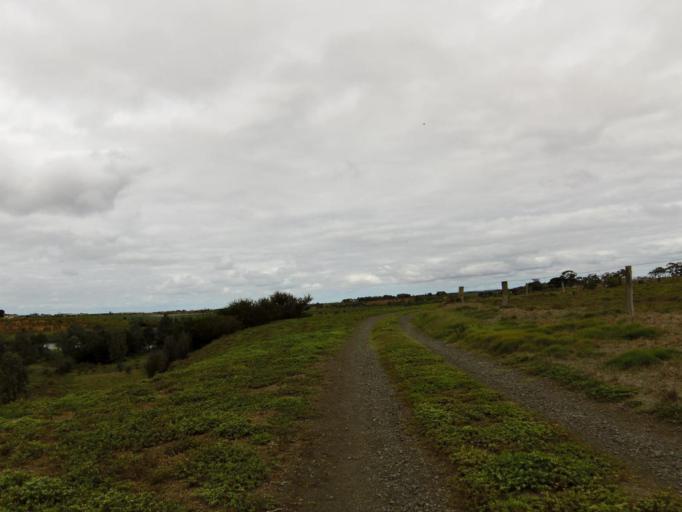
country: AU
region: Victoria
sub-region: Wyndham
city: Werribee
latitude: -37.9446
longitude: 144.6652
